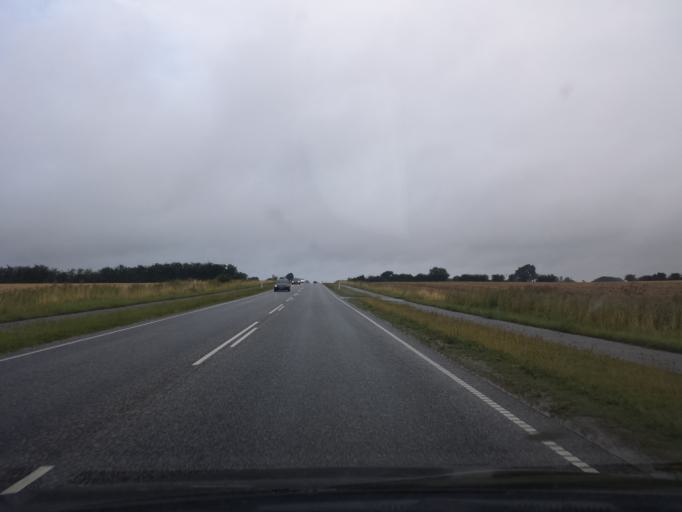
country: DK
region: South Denmark
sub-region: Sonderborg Kommune
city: Augustenborg
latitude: 54.9570
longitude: 9.8997
